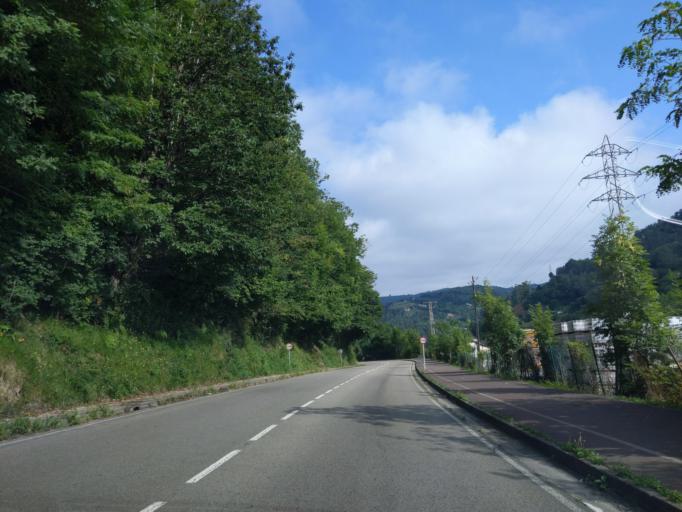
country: ES
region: Asturias
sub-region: Province of Asturias
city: El entrego
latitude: 43.2776
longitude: -5.6184
